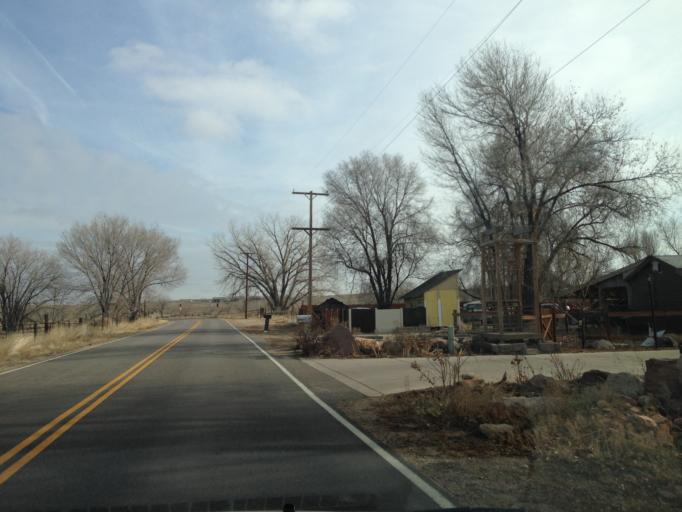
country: US
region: Colorado
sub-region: Boulder County
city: Lafayette
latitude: 39.9924
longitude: -105.0636
